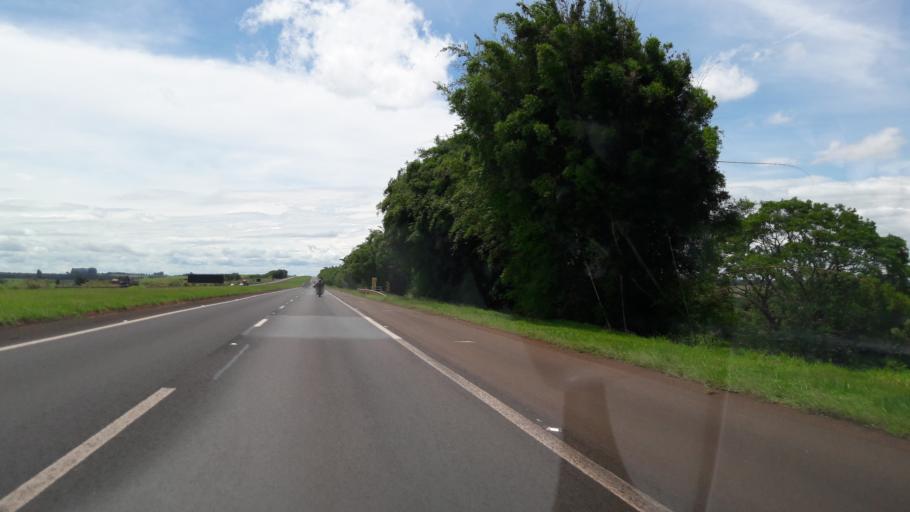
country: BR
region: Sao Paulo
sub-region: Avare
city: Avare
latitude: -22.9515
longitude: -48.8772
